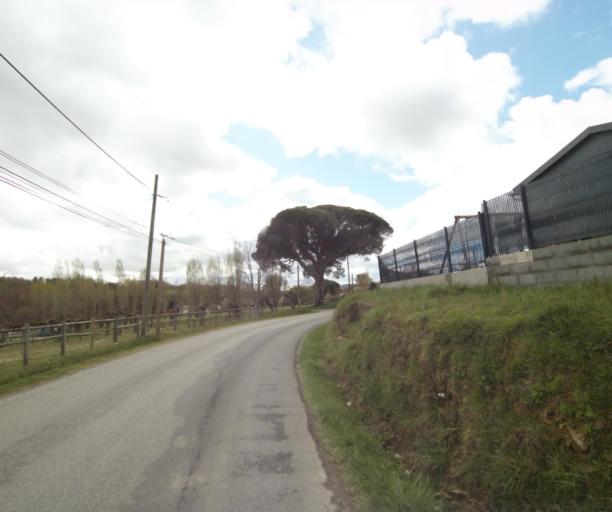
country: FR
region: Midi-Pyrenees
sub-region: Departement de l'Ariege
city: Saverdun
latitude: 43.2254
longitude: 1.5719
